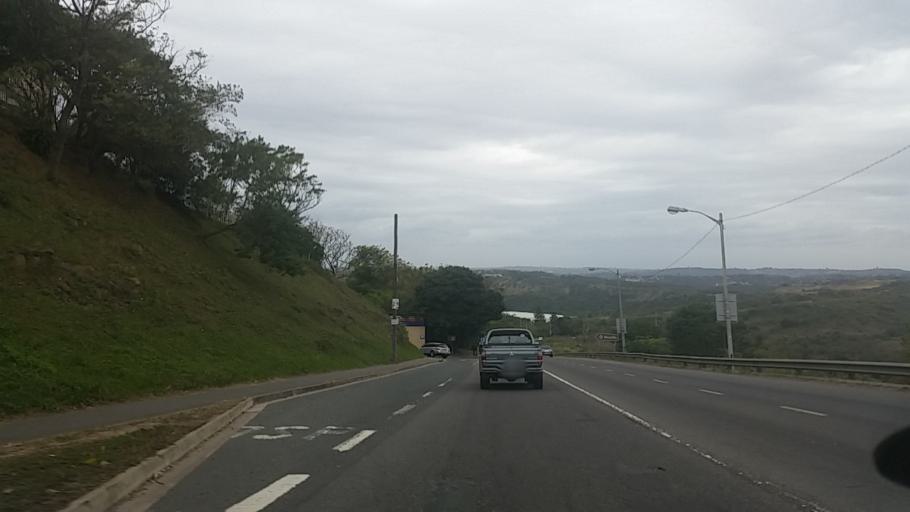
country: ZA
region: KwaZulu-Natal
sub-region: eThekwini Metropolitan Municipality
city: Berea
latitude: -29.8523
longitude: 30.9322
